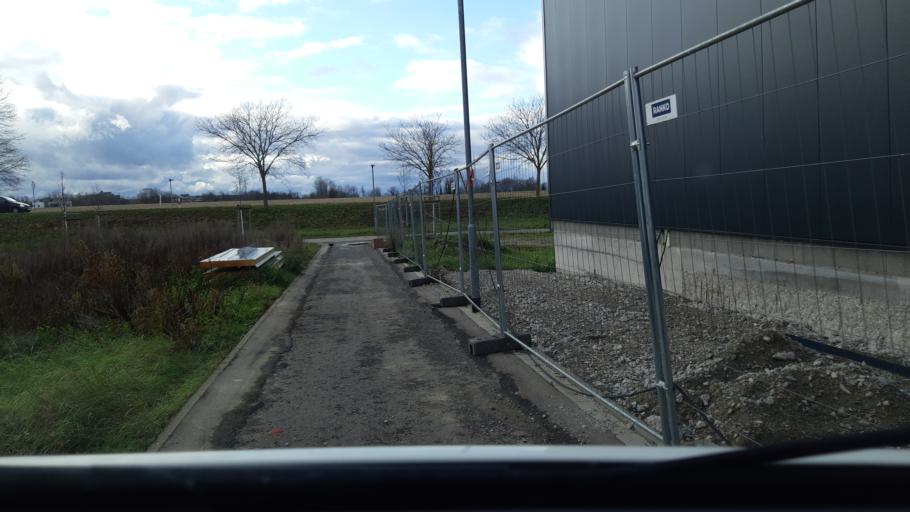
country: DE
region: Baden-Wuerttemberg
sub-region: Freiburg Region
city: Bad Krozingen
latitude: 47.9282
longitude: 7.7011
